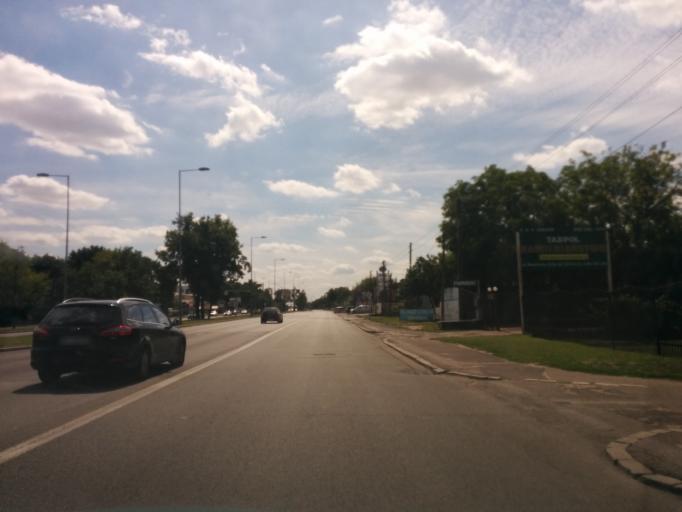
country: PL
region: Masovian Voivodeship
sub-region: Warszawa
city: Bialoleka
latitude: 52.3289
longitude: 20.9669
